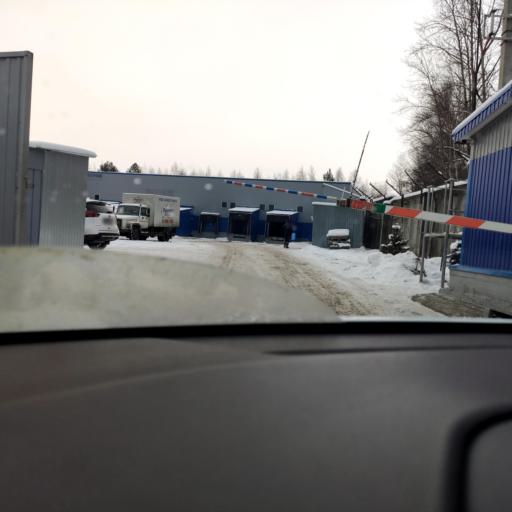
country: RU
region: Tatarstan
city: Osinovo
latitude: 55.8886
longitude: 48.8285
